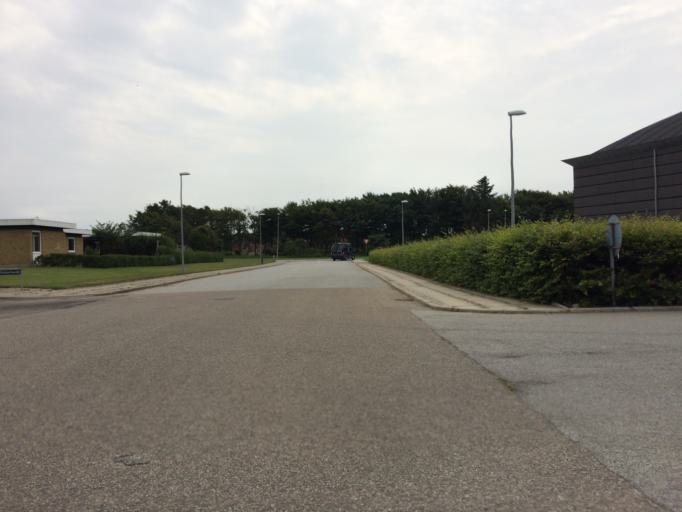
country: DK
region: Central Jutland
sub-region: Holstebro Kommune
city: Ulfborg
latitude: 56.2778
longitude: 8.3203
